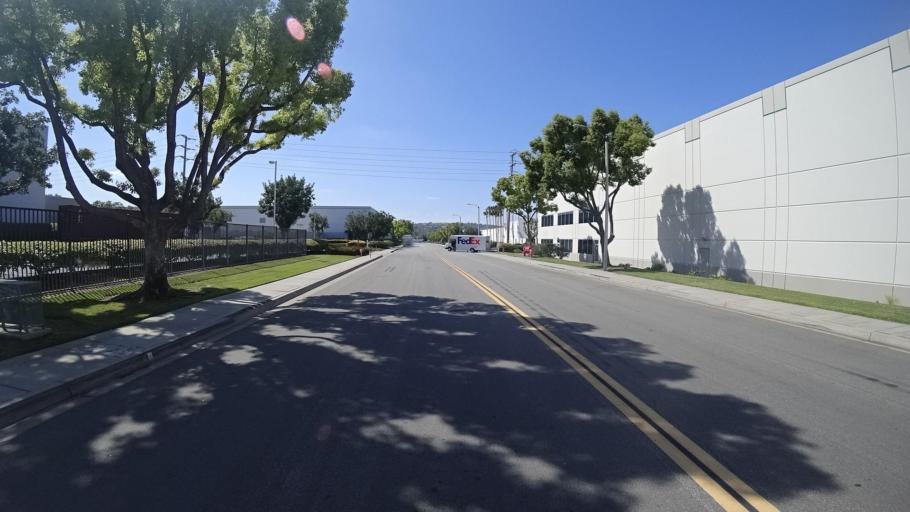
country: US
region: California
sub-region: Los Angeles County
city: Walnut
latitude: 34.0133
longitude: -117.8481
